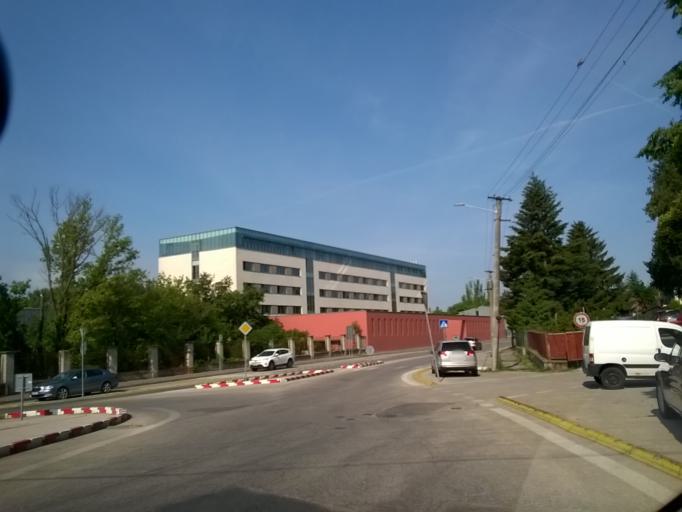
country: SK
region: Nitriansky
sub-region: Okres Nitra
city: Nitra
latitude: 48.3233
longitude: 18.0951
